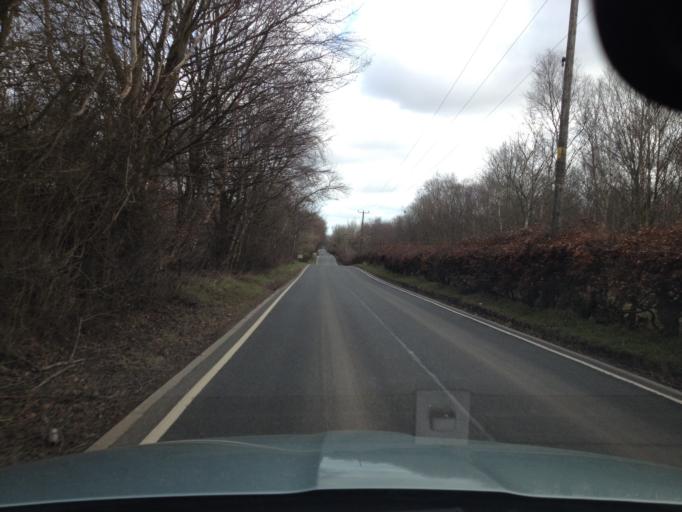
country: GB
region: Scotland
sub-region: West Lothian
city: Broxburn
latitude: 55.9144
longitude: -3.4691
